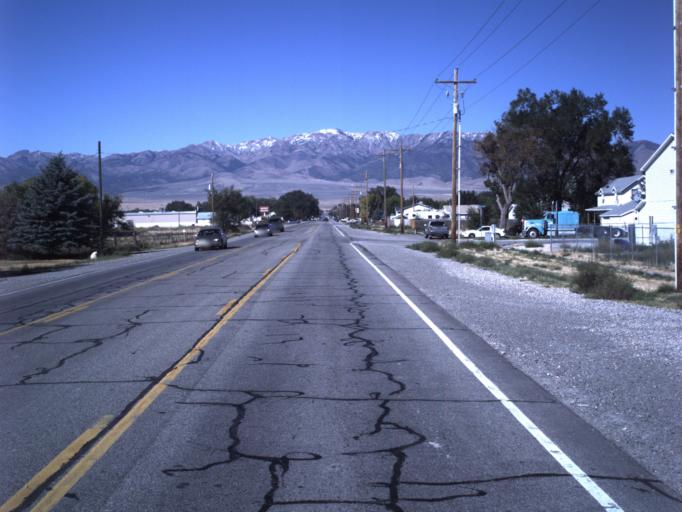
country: US
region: Utah
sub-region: Tooele County
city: Grantsville
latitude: 40.5997
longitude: -112.4353
